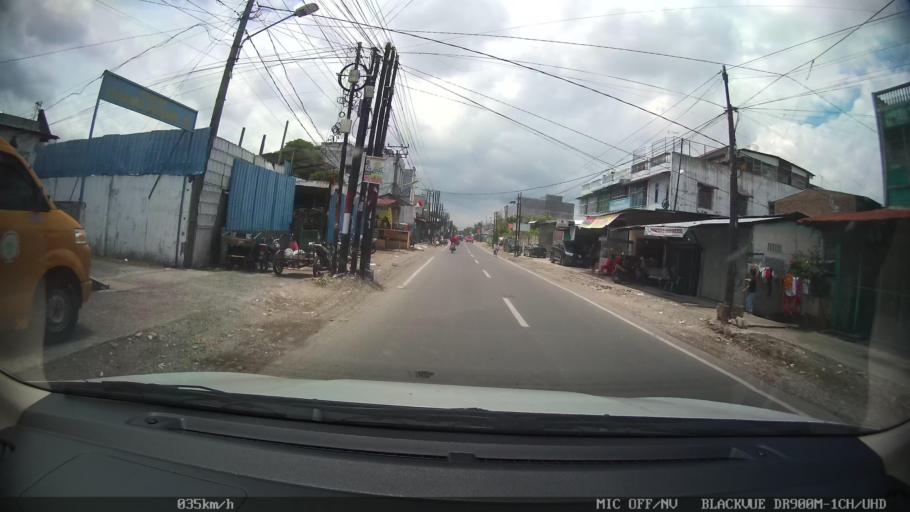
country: ID
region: North Sumatra
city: Medan
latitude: 3.6160
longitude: 98.6933
